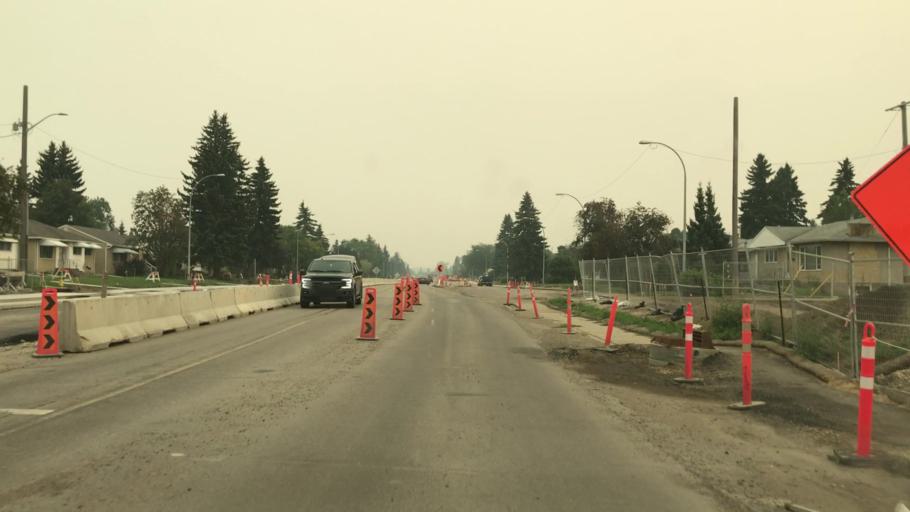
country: CA
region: Alberta
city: Edmonton
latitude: 53.5122
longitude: -113.4552
